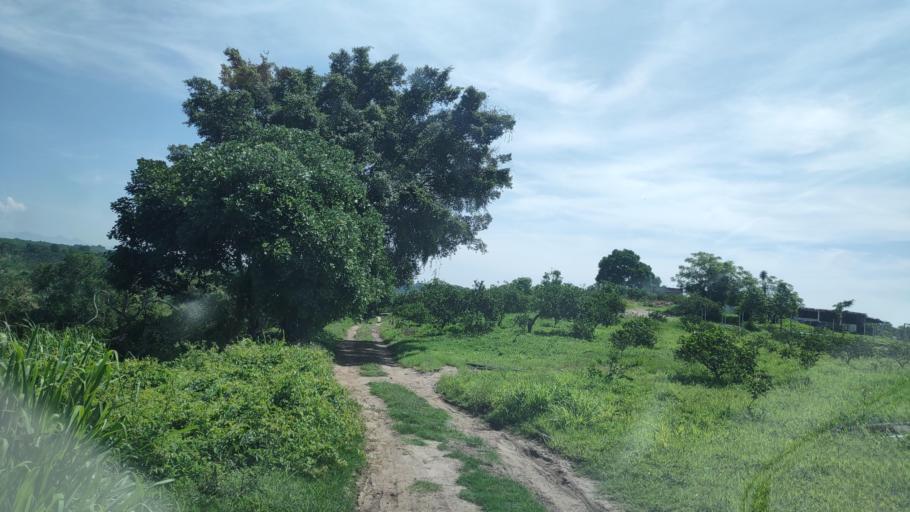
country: MX
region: Veracruz
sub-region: Emiliano Zapata
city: Dos Rios
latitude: 19.4292
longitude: -96.7928
